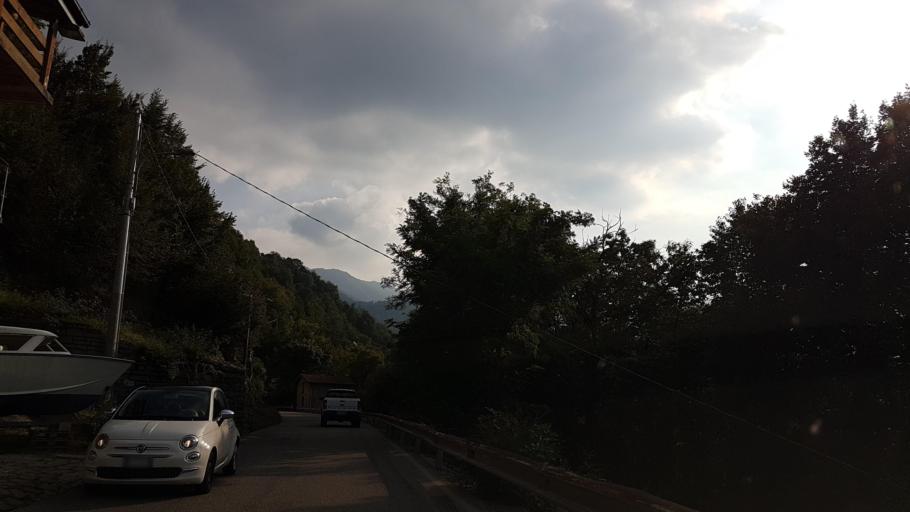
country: IT
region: Lombardy
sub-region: Provincia di Como
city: Pognana Lario
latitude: 45.8712
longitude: 9.1580
